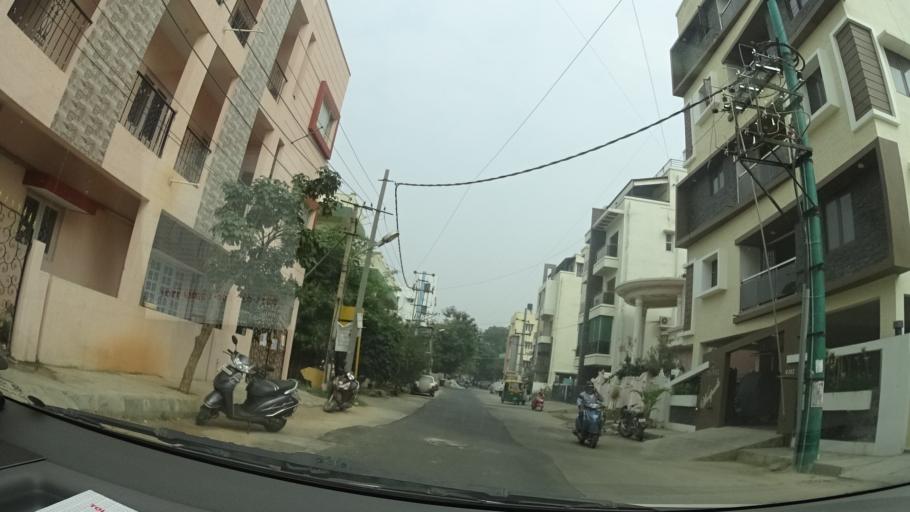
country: IN
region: Karnataka
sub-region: Bangalore Urban
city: Bangalore
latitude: 13.0223
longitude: 77.6282
